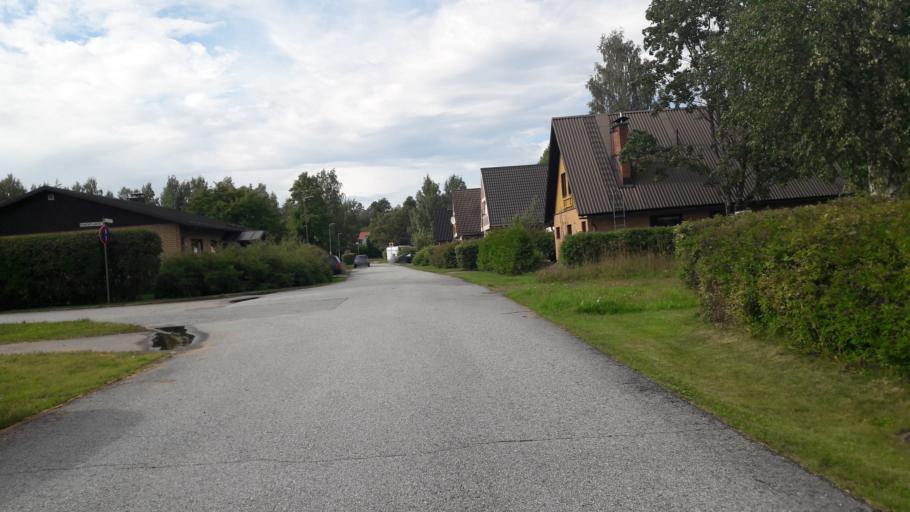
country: FI
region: North Karelia
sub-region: Joensuu
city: Joensuu
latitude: 62.5803
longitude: 29.8104
